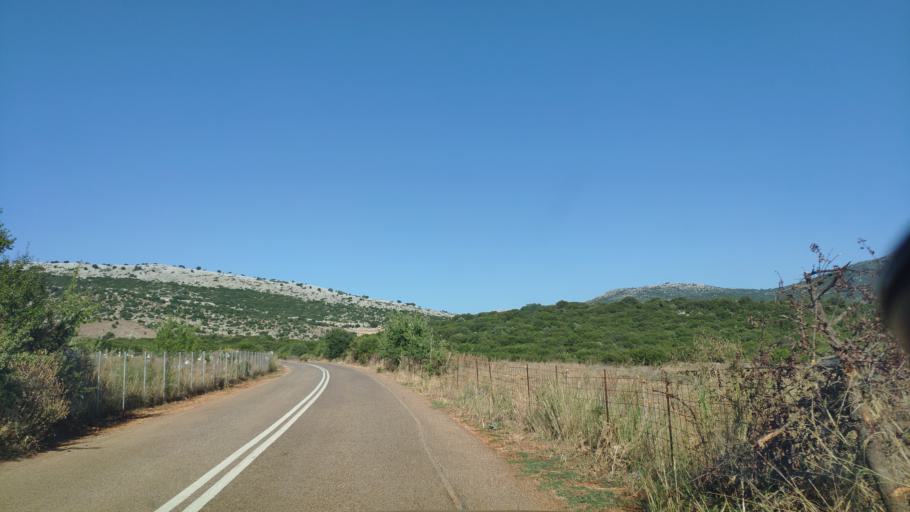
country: GR
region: West Greece
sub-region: Nomos Aitolias kai Akarnanias
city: Archontochorion
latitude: 38.6912
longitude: 21.0510
